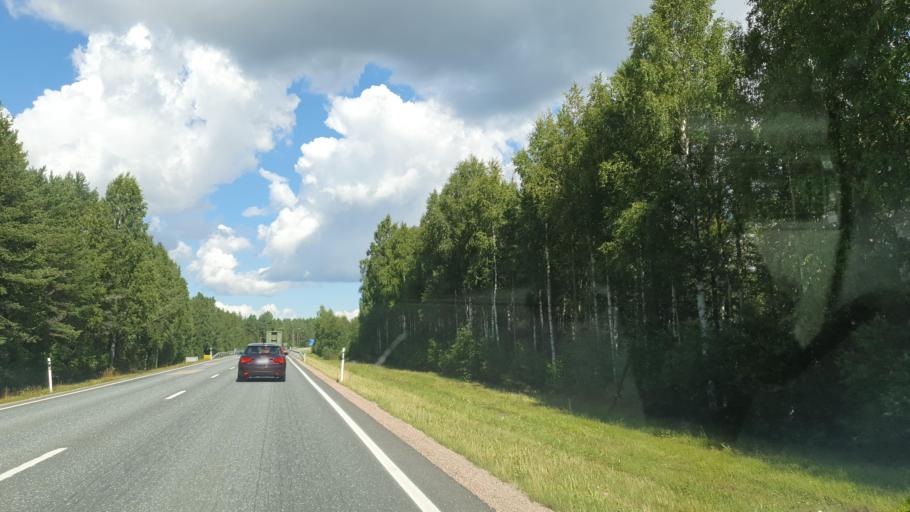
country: FI
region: Kainuu
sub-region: Kajaani
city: Kajaani
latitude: 64.1129
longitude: 27.4485
